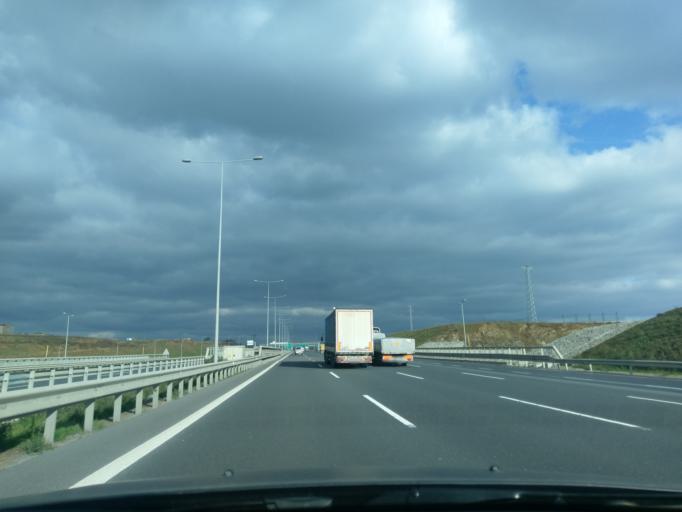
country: TR
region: Istanbul
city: Basaksehir
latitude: 41.1031
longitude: 28.8143
